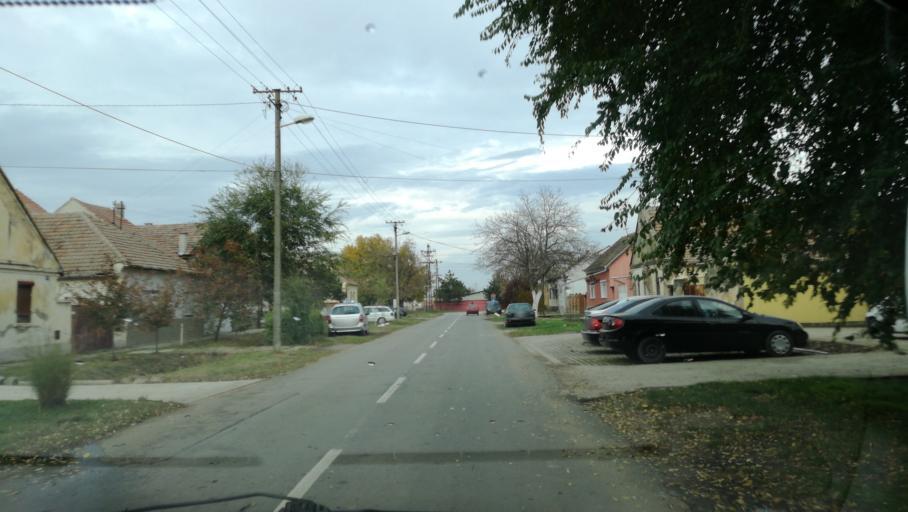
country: RS
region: Autonomna Pokrajina Vojvodina
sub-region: Severnobanatski Okrug
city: Kikinda
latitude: 45.8425
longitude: 20.4799
